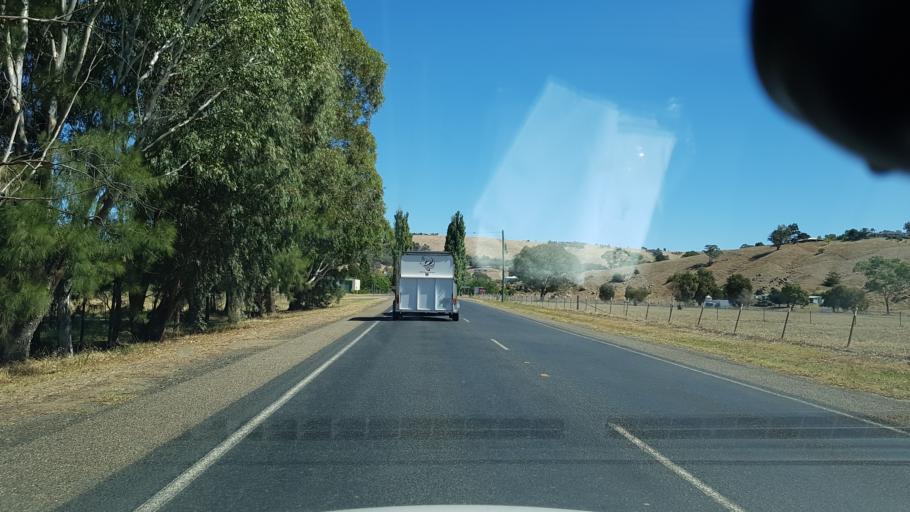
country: AU
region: New South Wales
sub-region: Gundagai
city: Gundagai
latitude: -34.8229
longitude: 148.3338
